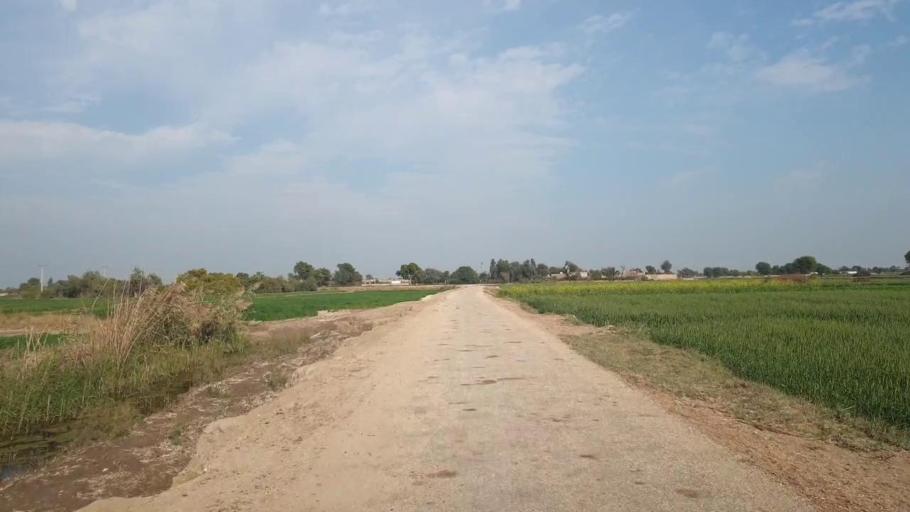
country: PK
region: Sindh
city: Shahdadpur
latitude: 26.0399
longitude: 68.5289
